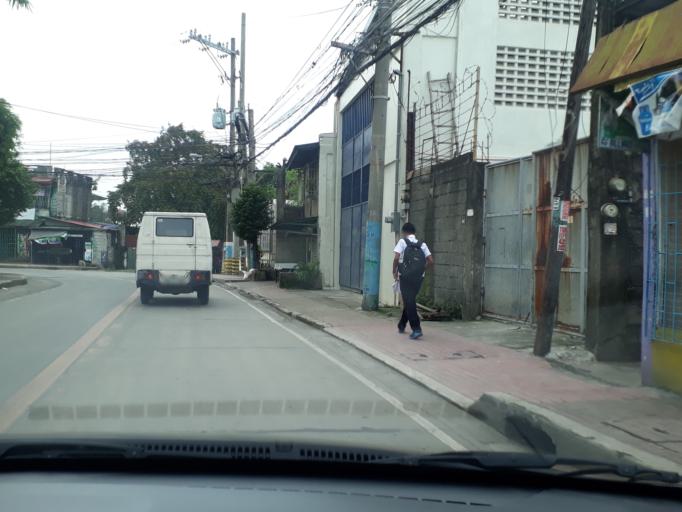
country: PH
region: Calabarzon
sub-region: Province of Rizal
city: Valenzuela
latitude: 14.7153
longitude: 120.9806
